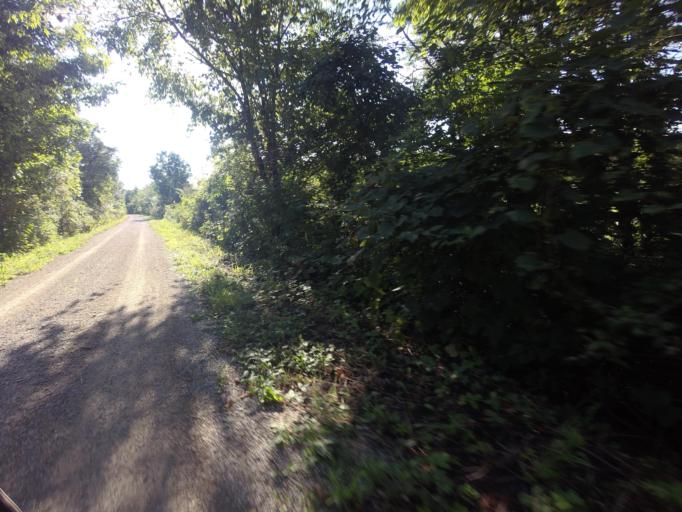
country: CA
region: Ontario
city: Huron East
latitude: 43.7376
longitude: -81.4596
